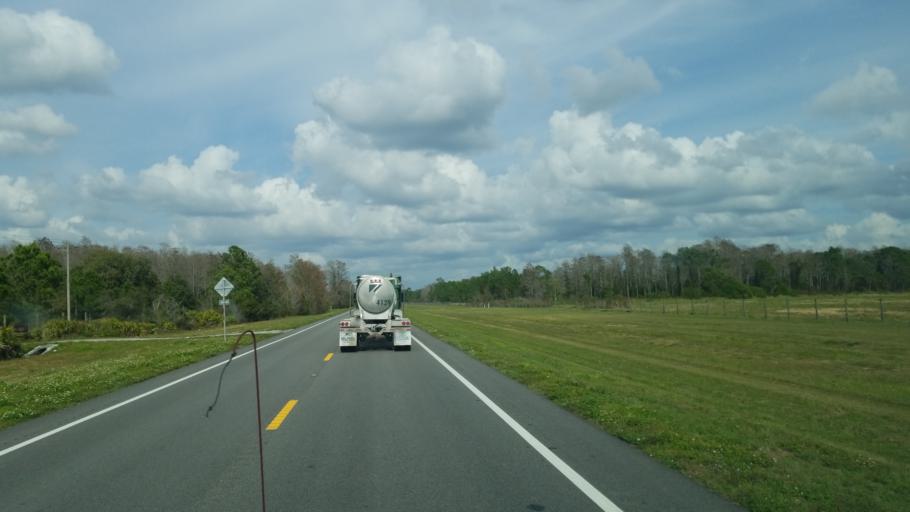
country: US
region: Florida
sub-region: Indian River County
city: Fellsmere
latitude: 27.7342
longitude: -80.9092
